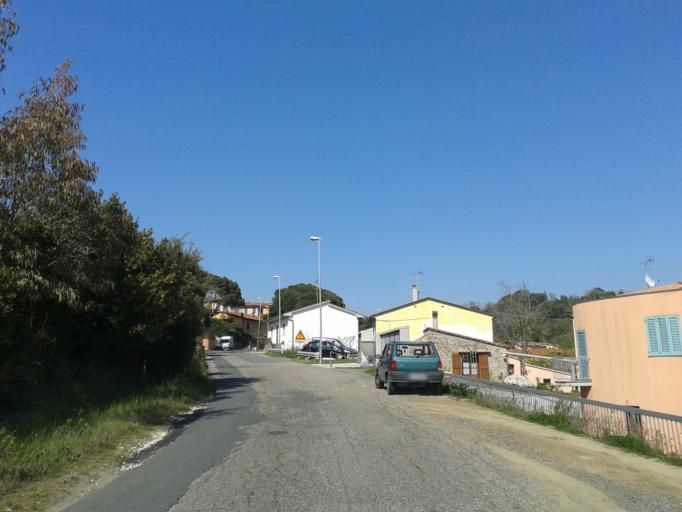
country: IT
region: Tuscany
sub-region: Provincia di Livorno
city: Quercianella
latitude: 43.4604
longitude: 10.4093
